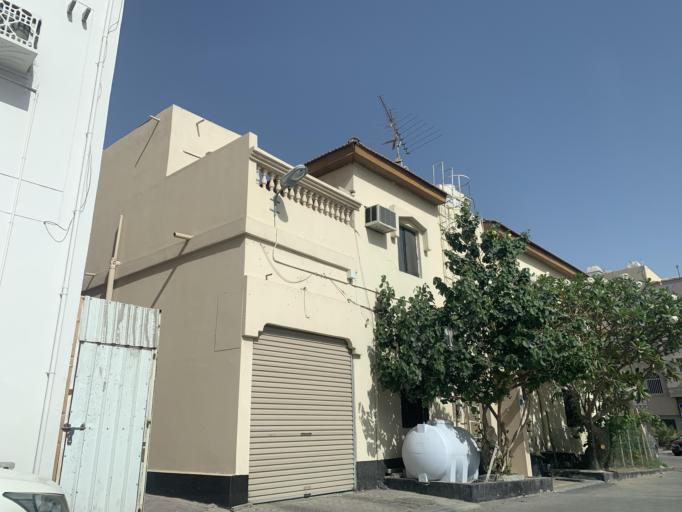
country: BH
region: Northern
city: Sitrah
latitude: 26.1628
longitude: 50.6140
